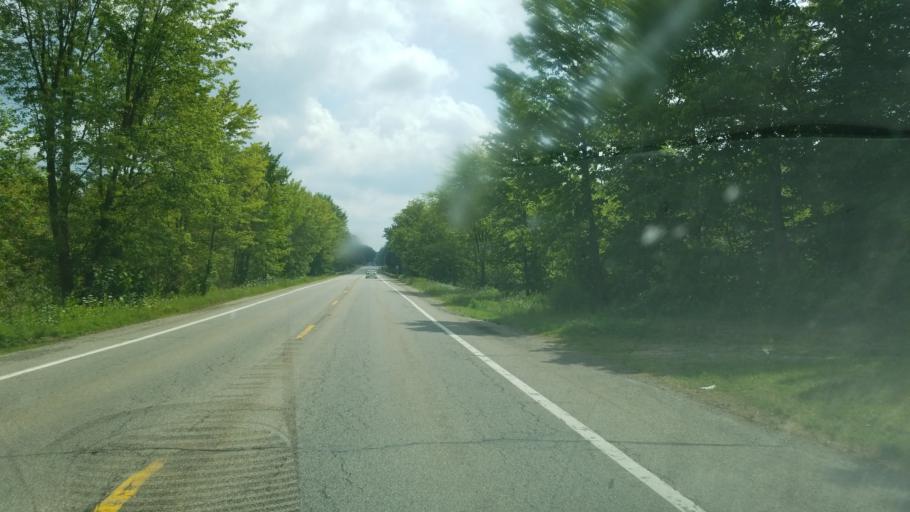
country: US
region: Michigan
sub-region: Kent County
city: Sparta
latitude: 43.2198
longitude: -85.6831
